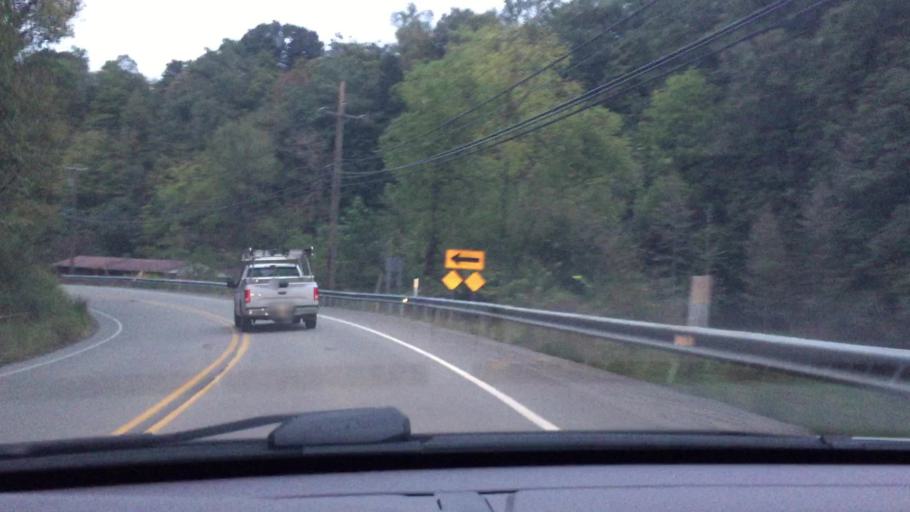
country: US
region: Pennsylvania
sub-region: Westmoreland County
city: West Newton
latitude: 40.2000
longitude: -79.7902
